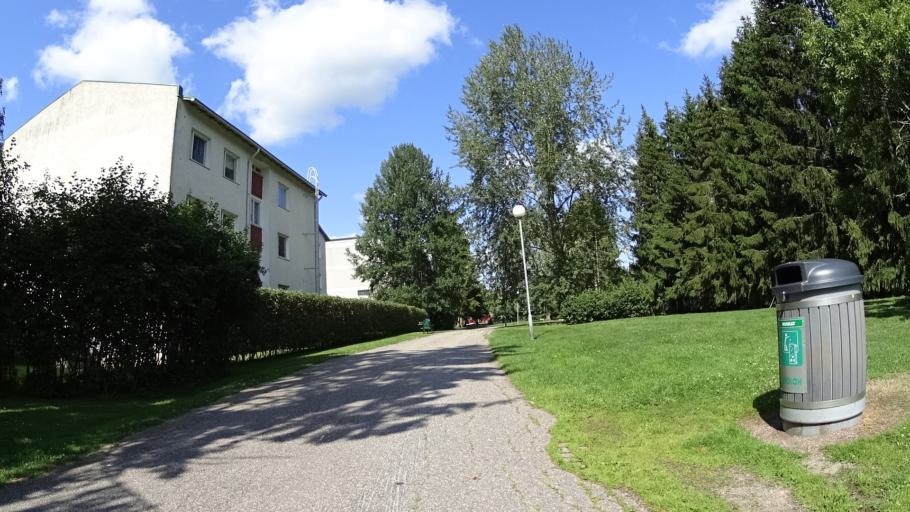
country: FI
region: Uusimaa
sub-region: Helsinki
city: Jaervenpaeae
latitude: 60.4735
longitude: 25.0832
